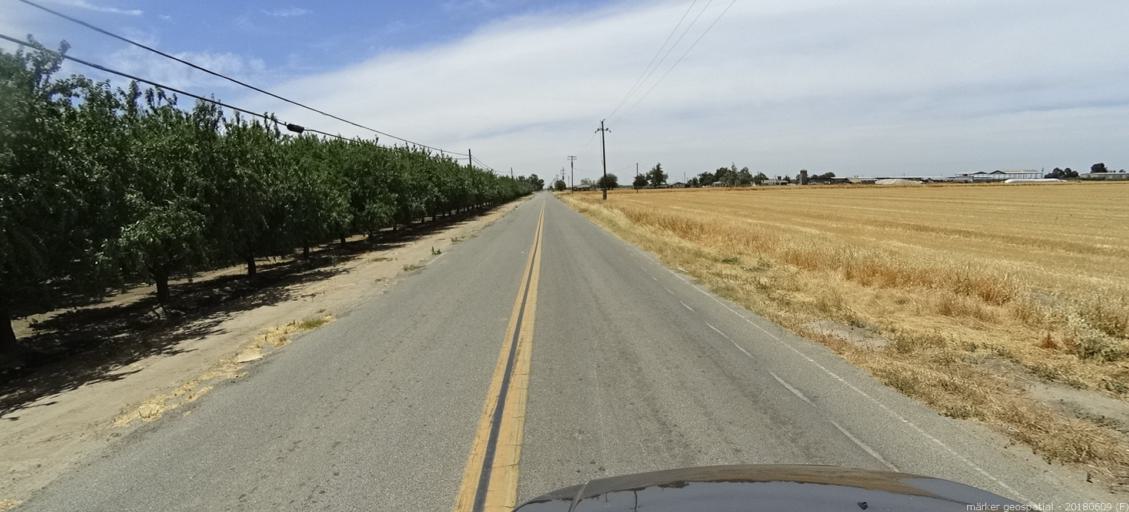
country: US
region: California
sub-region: Madera County
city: Parkwood
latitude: 36.9093
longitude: -120.0926
